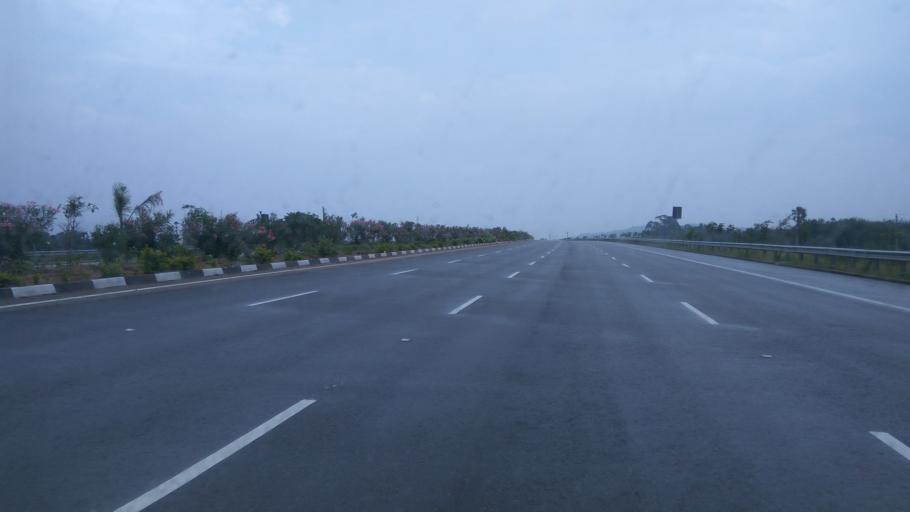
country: IN
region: Telangana
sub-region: Rangareddi
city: Ghatkesar
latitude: 17.4616
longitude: 78.6702
